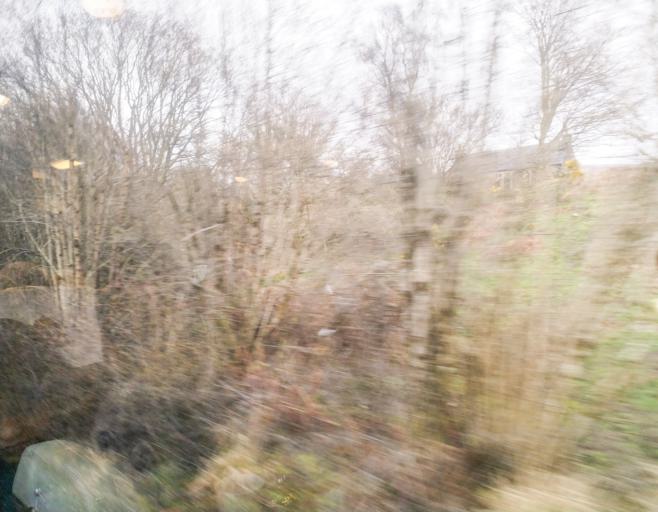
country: GB
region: Scotland
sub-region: Highland
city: Spean Bridge
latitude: 56.8880
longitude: -4.8593
